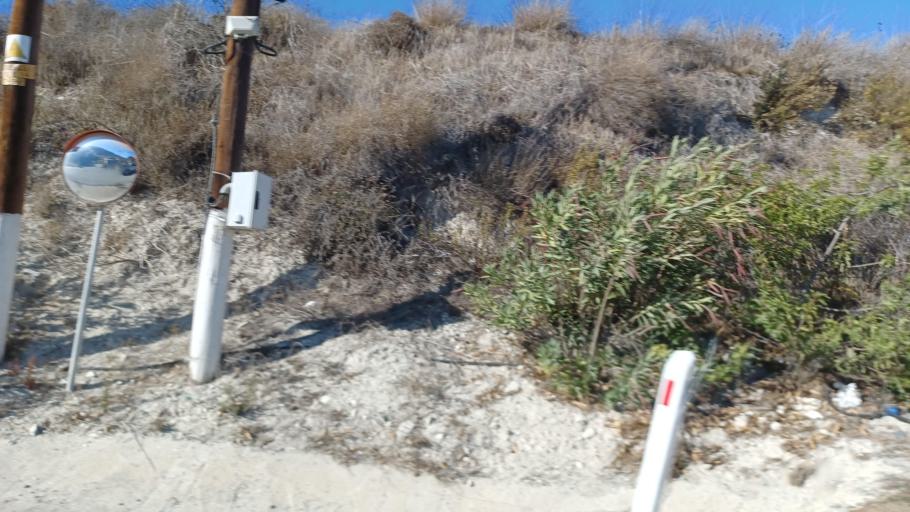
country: CY
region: Limassol
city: Pyrgos
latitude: 34.7711
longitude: 33.2427
